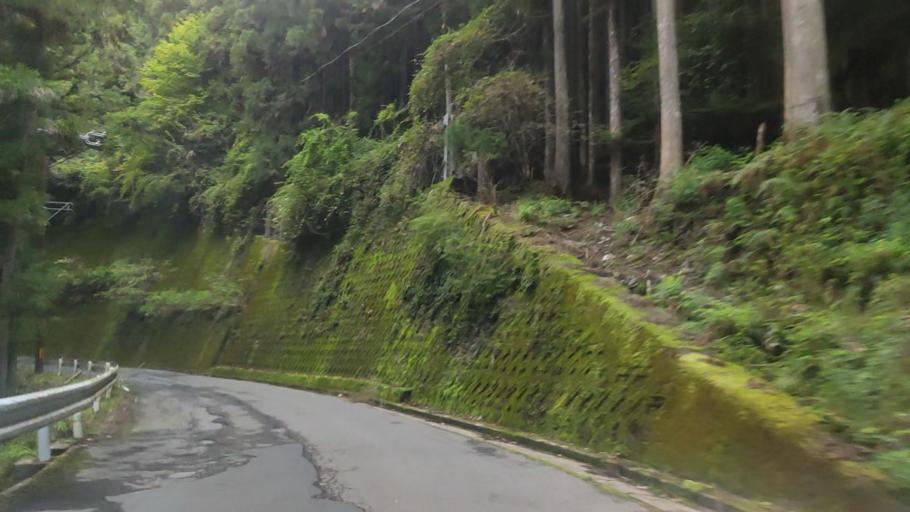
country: JP
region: Wakayama
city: Koya
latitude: 34.2356
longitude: 135.6490
